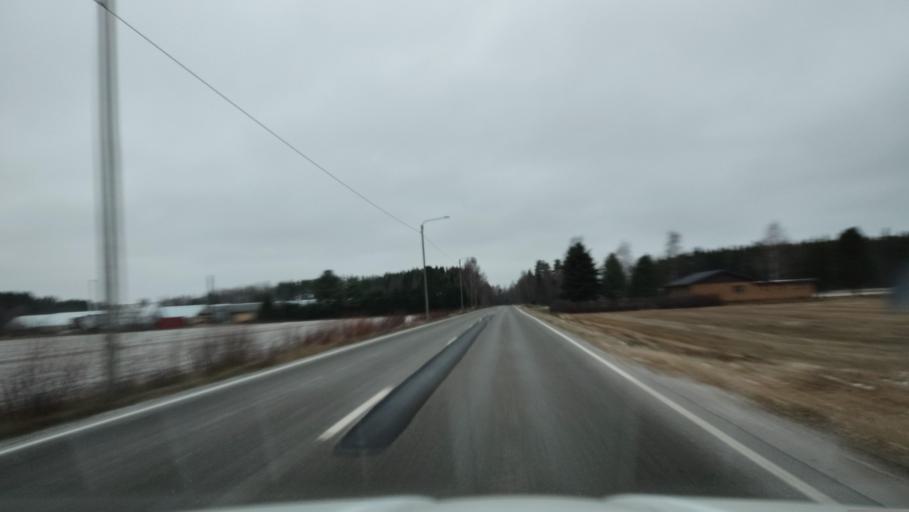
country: FI
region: Southern Ostrobothnia
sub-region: Suupohja
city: Karijoki
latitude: 62.2382
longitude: 21.6073
